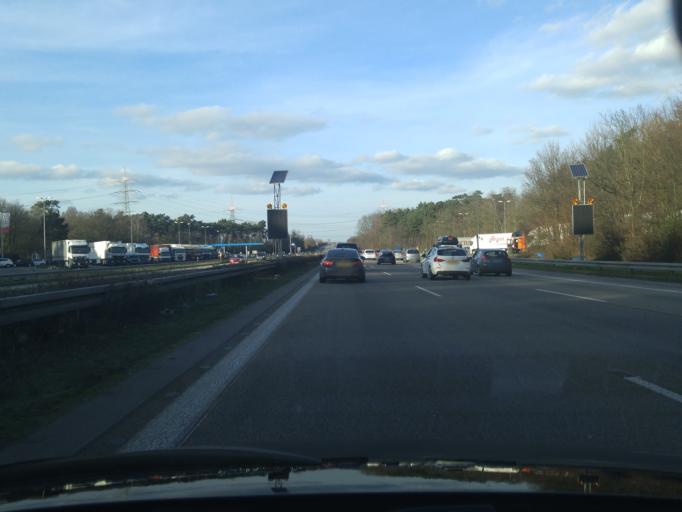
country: DE
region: North Rhine-Westphalia
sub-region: Regierungsbezirk Dusseldorf
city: Hilden
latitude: 51.1569
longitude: 6.9636
